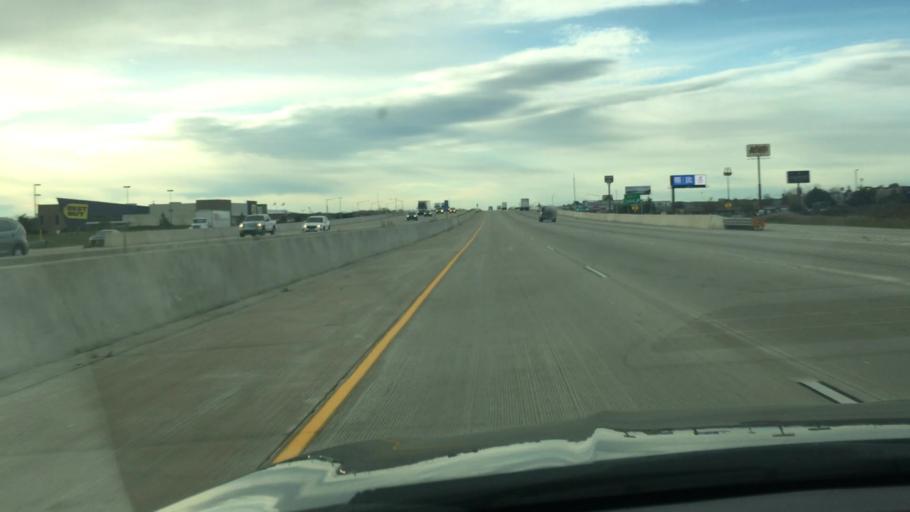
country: US
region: Wisconsin
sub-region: Kenosha County
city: Pleasant Prairie
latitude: 42.5744
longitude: -87.9530
